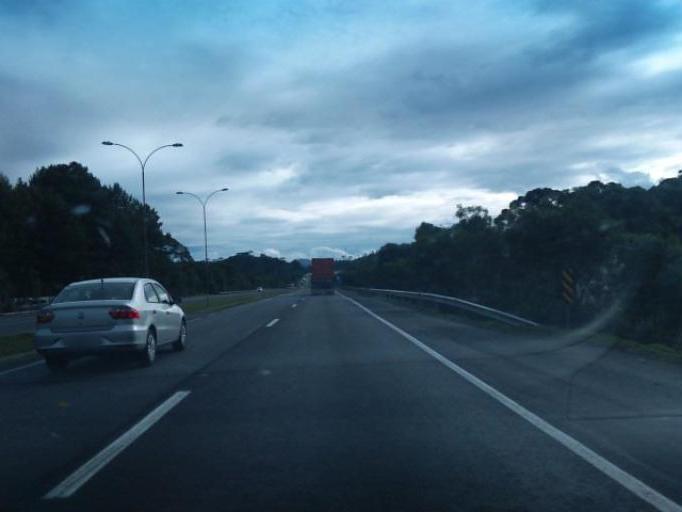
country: BR
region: Parana
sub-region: Campina Grande Do Sul
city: Campina Grande do Sul
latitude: -25.2804
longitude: -48.9269
